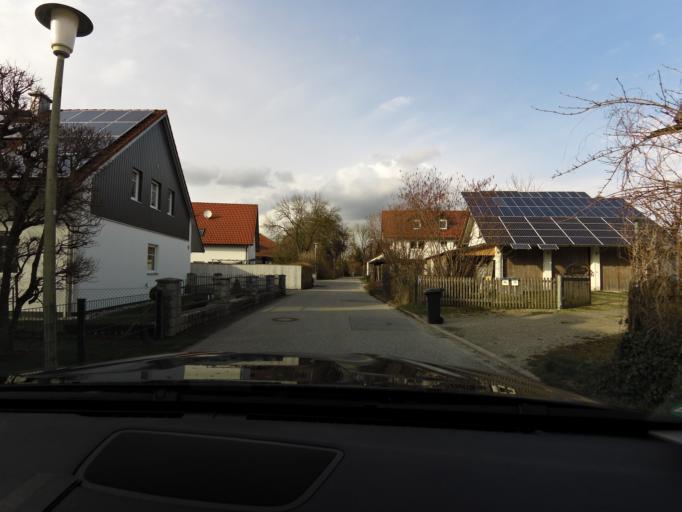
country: DE
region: Bavaria
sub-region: Lower Bavaria
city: Eching
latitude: 48.4955
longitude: 12.0295
